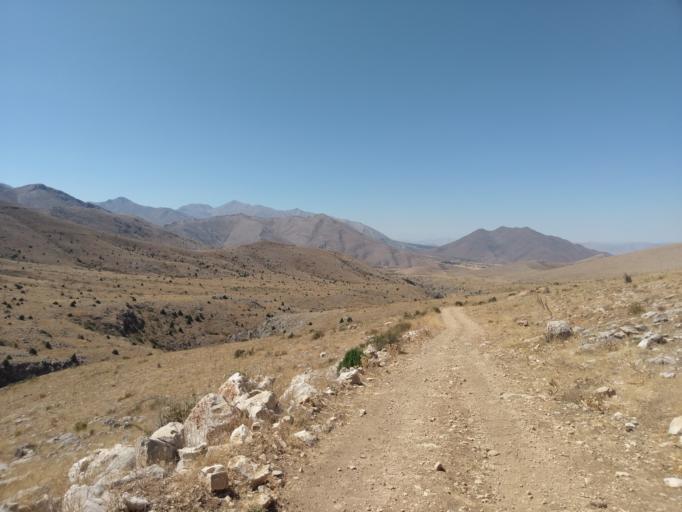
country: TR
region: Kayseri
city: Toklar
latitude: 38.4268
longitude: 36.1457
